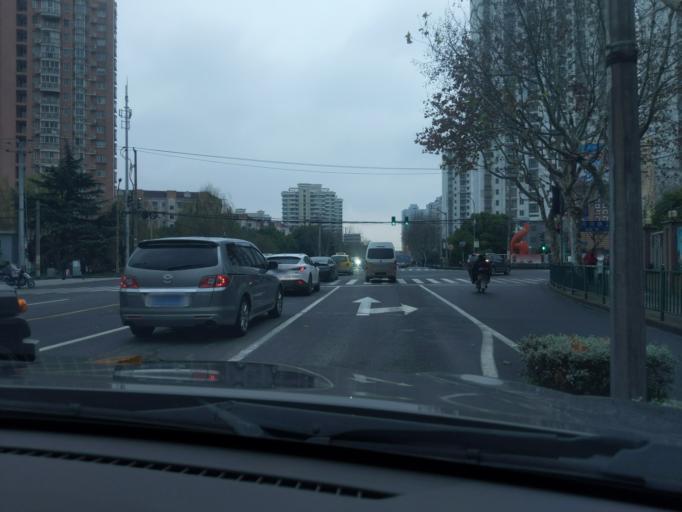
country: CN
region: Shanghai Shi
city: Huamu
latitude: 31.1835
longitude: 121.5054
